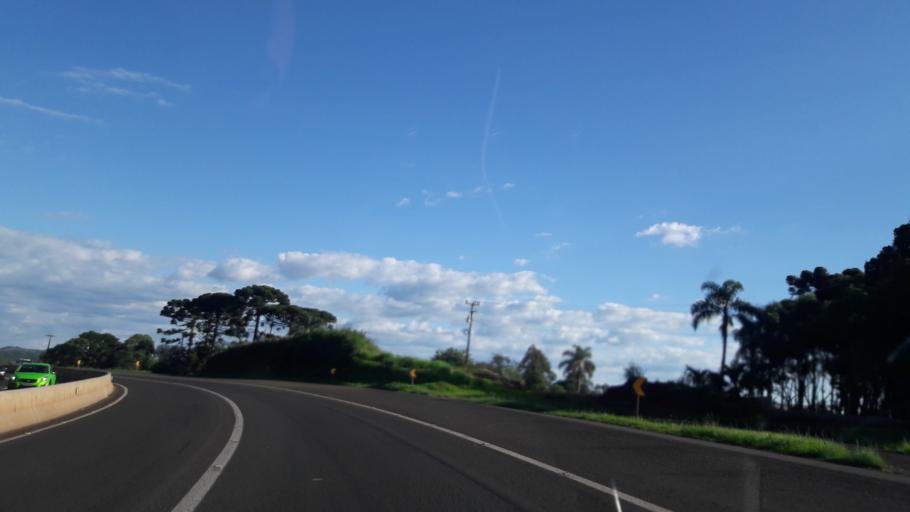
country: BR
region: Parana
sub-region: Guarapuava
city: Guarapuava
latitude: -25.3477
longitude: -51.3914
